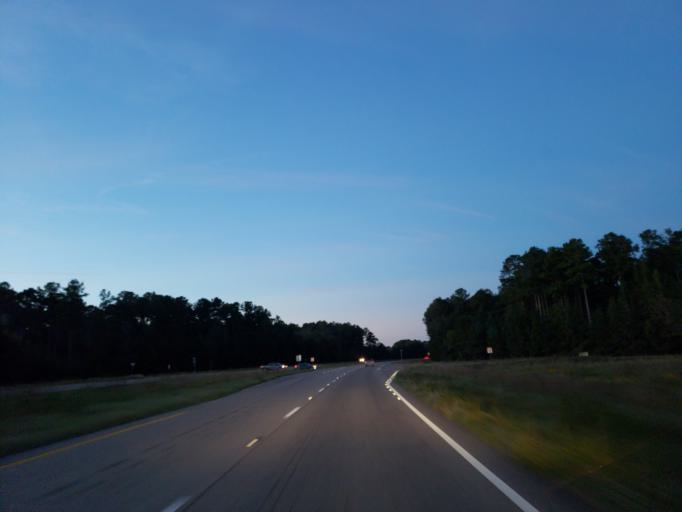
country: US
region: Mississippi
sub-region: Clarke County
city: Quitman
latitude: 31.8564
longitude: -88.7200
